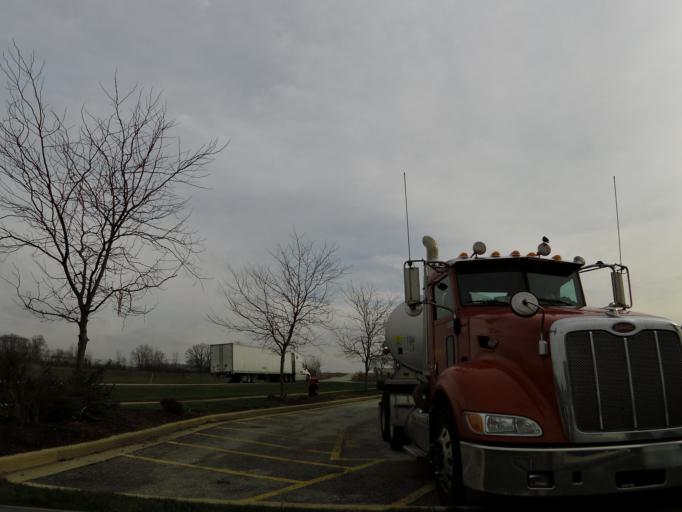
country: US
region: Indiana
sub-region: Shelby County
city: Shelbyville
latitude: 39.5840
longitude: -85.8180
